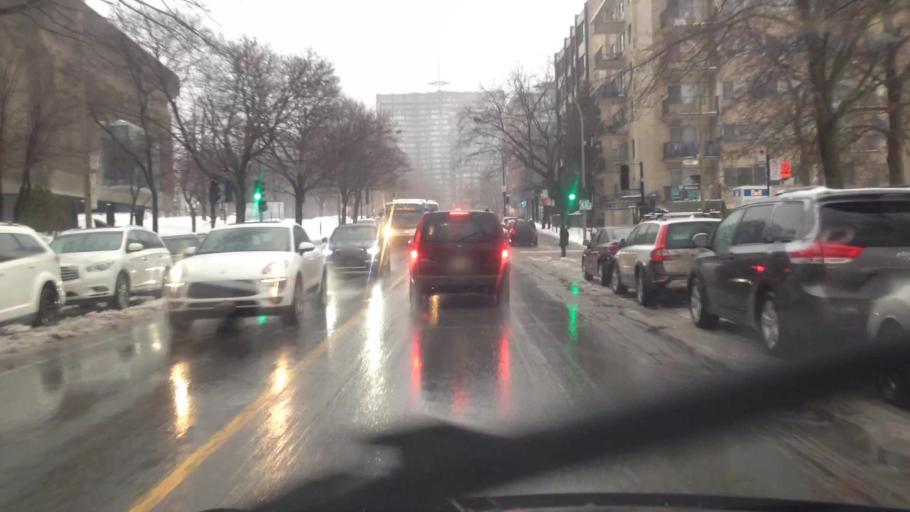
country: CA
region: Quebec
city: Westmount
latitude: 45.4974
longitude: -73.6191
